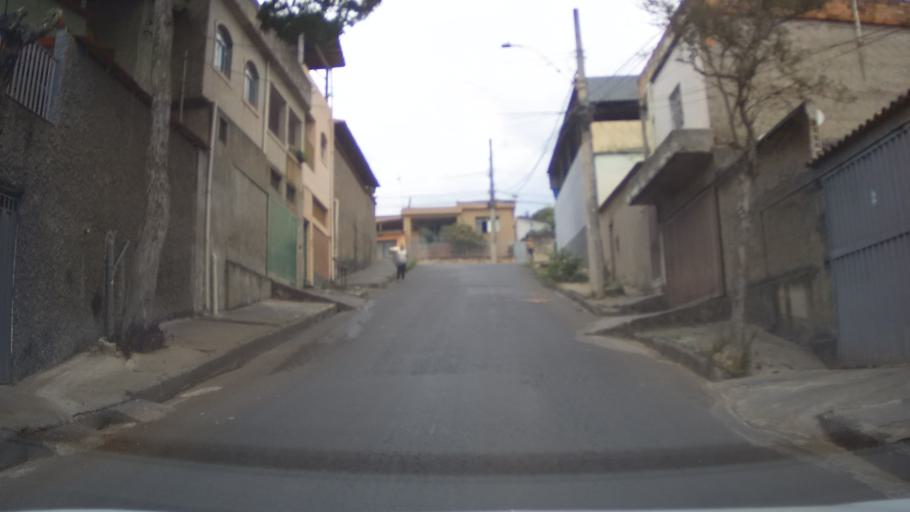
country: BR
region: Minas Gerais
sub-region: Belo Horizonte
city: Belo Horizonte
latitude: -19.8764
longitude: -43.9232
